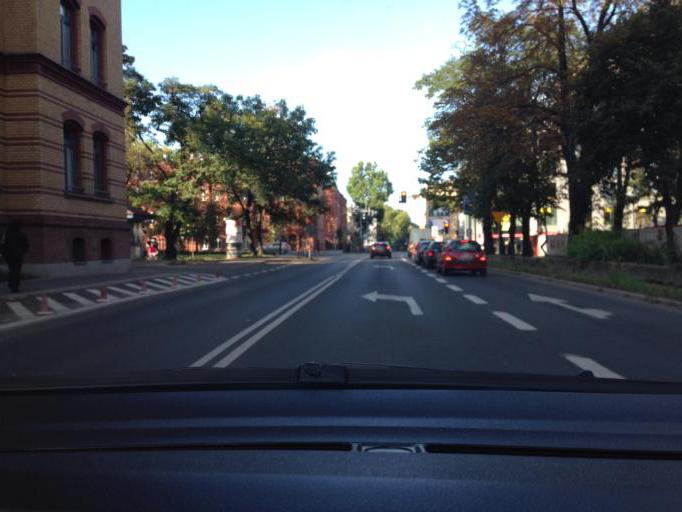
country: PL
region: Greater Poland Voivodeship
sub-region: Poznan
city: Poznan
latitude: 52.4071
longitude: 16.9012
